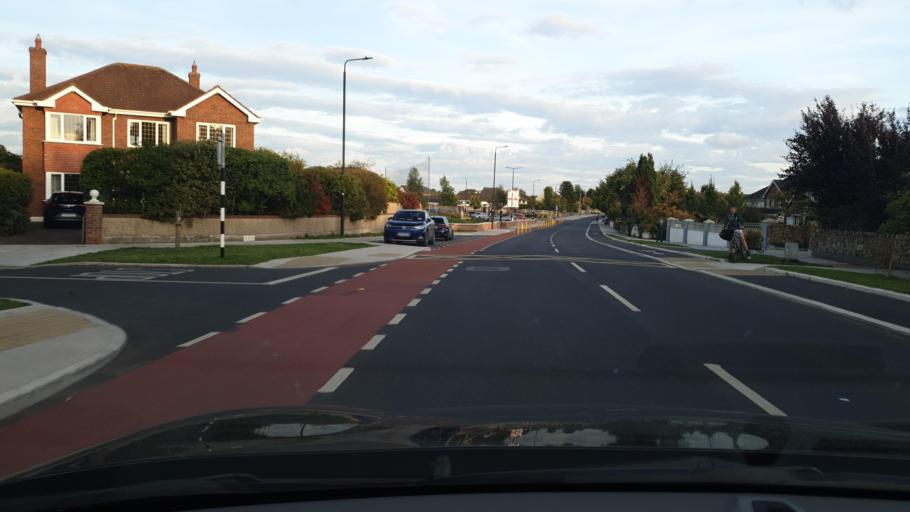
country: IE
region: Leinster
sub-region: An Mhi
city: Ashbourne
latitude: 53.5087
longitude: -6.3905
